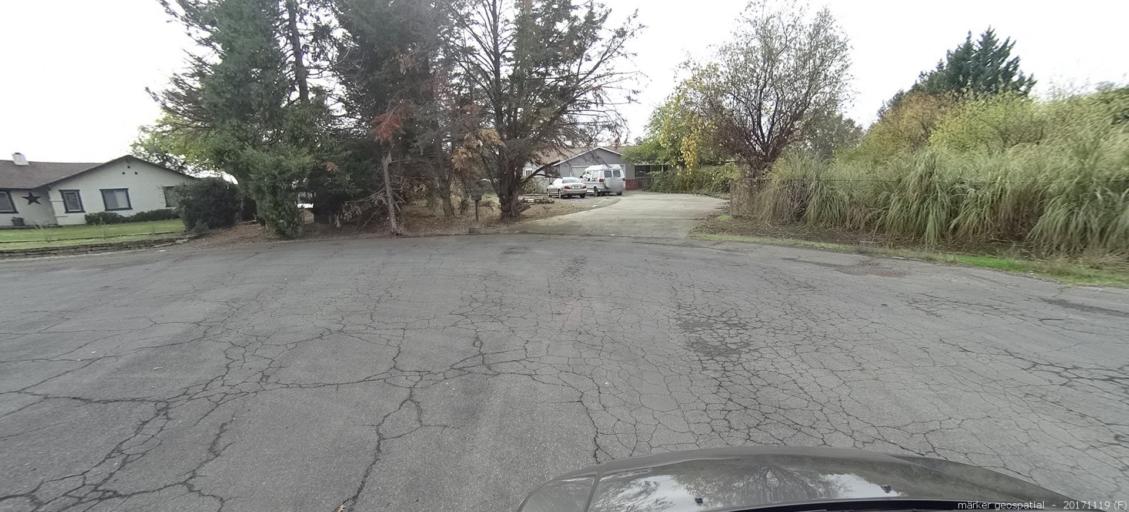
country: US
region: California
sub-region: Shasta County
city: Anderson
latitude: 40.4774
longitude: -122.2706
